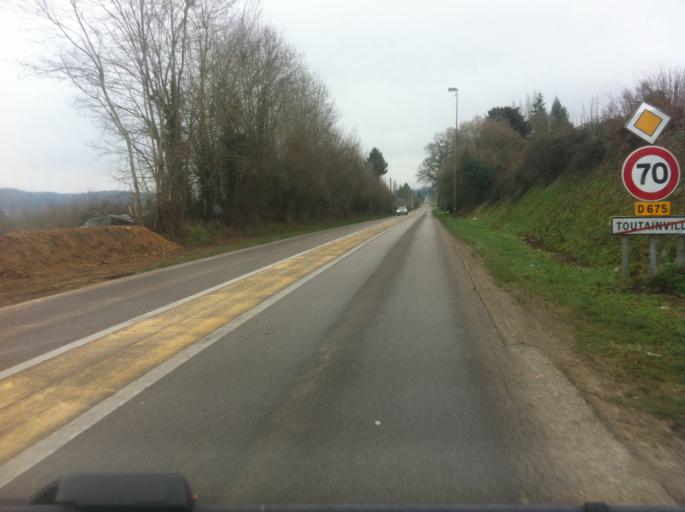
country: FR
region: Haute-Normandie
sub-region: Departement de l'Eure
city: Toutainville
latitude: 49.3619
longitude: 0.4714
